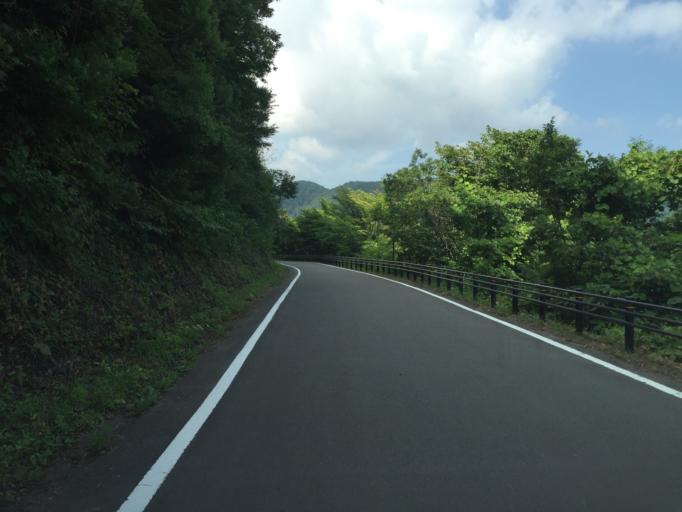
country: JP
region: Fukushima
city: Inawashiro
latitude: 37.4172
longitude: 140.1046
